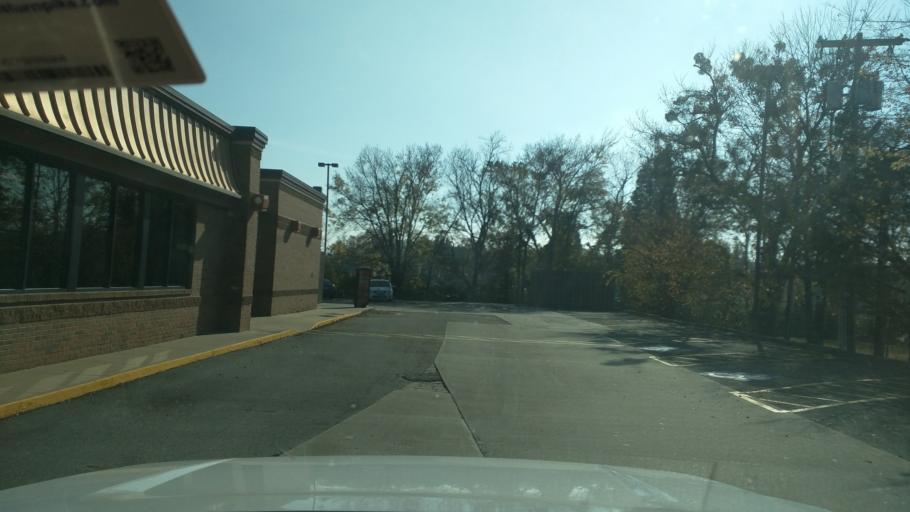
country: US
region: Arkansas
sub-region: Sebastian County
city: Barling
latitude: 35.3484
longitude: -94.3415
